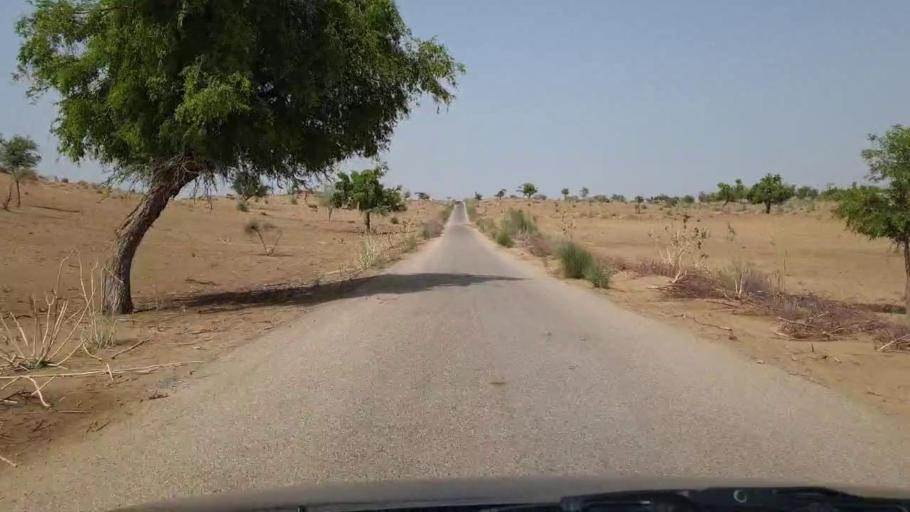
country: PK
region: Sindh
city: Chor
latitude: 25.4650
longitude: 70.4901
